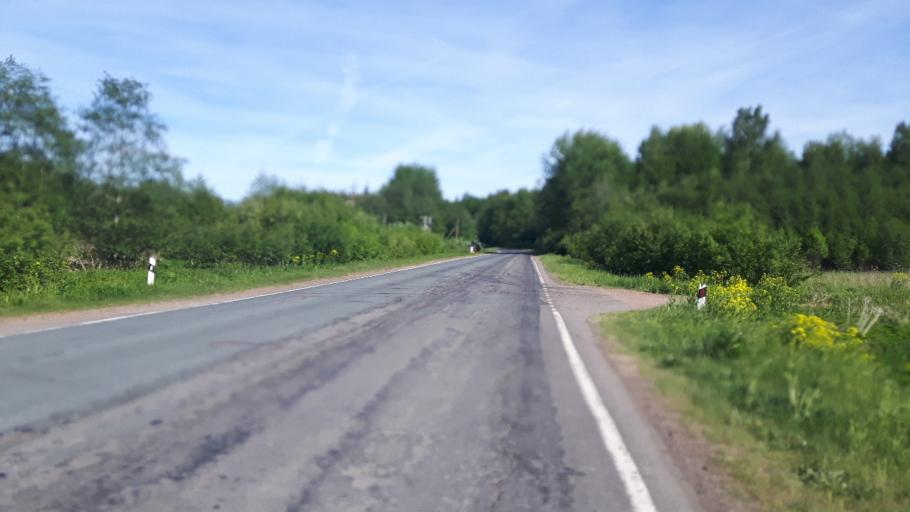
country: RU
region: Leningrad
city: Ivangorod
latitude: 59.4172
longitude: 28.3656
